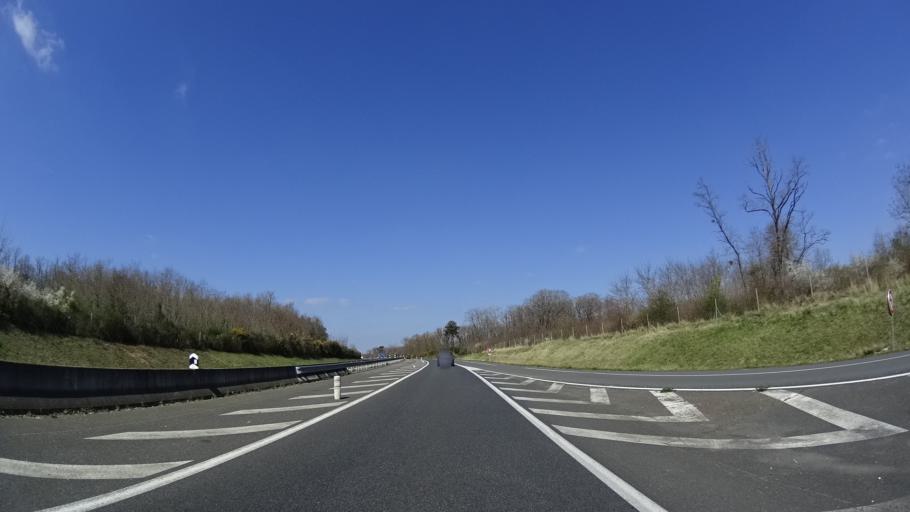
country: FR
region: Pays de la Loire
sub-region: Departement de Maine-et-Loire
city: Saint-Jean
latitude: 47.3022
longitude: -0.3903
